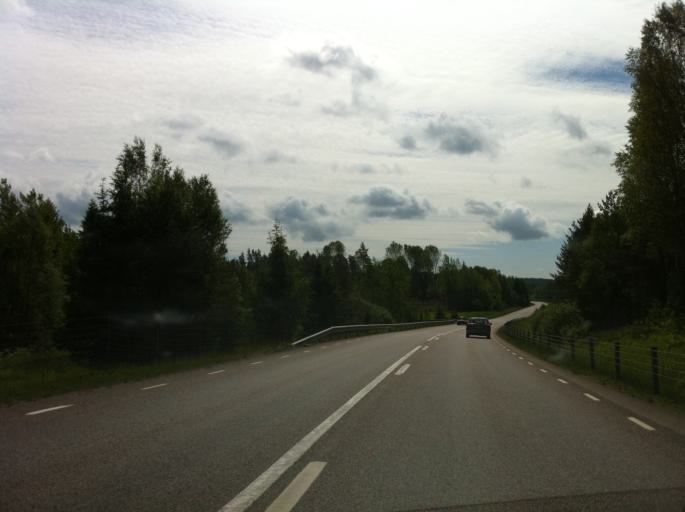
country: SE
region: Vaermland
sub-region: Saffle Kommun
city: Saeffle
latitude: 59.2192
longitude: 13.0111
